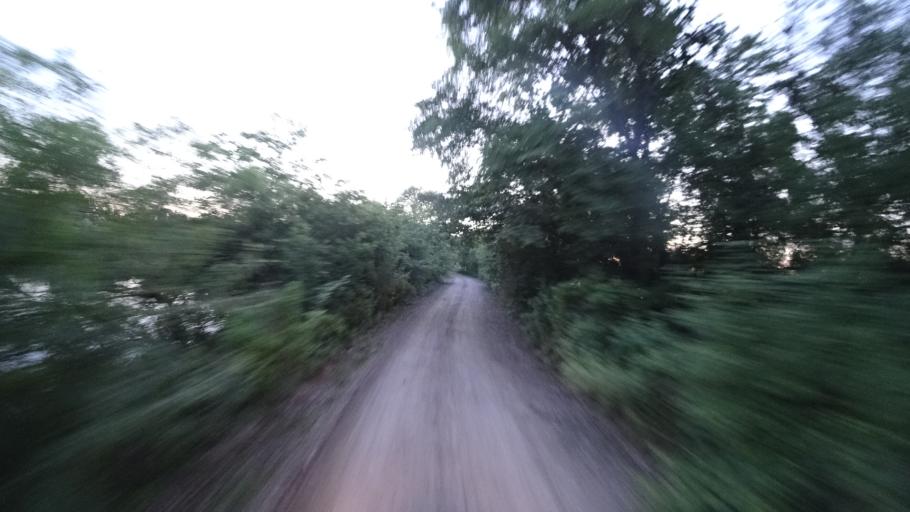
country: RU
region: Khabarovsk Krai
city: Khor
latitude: 47.8570
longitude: 134.9396
